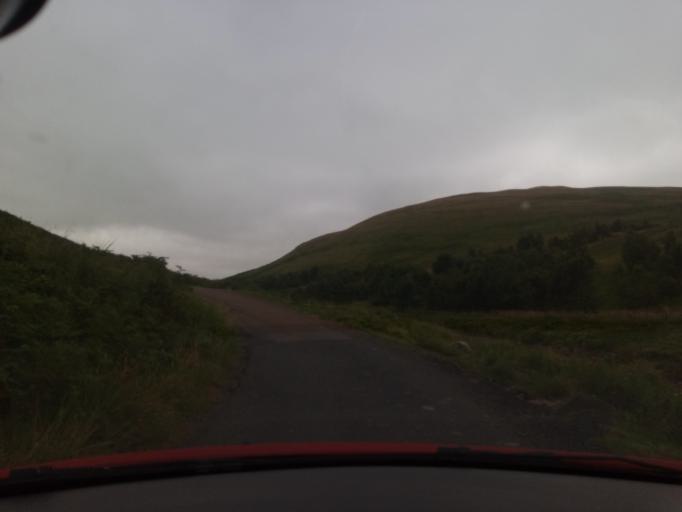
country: GB
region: England
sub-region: Northumberland
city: Rochester
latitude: 55.3649
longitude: -2.1937
